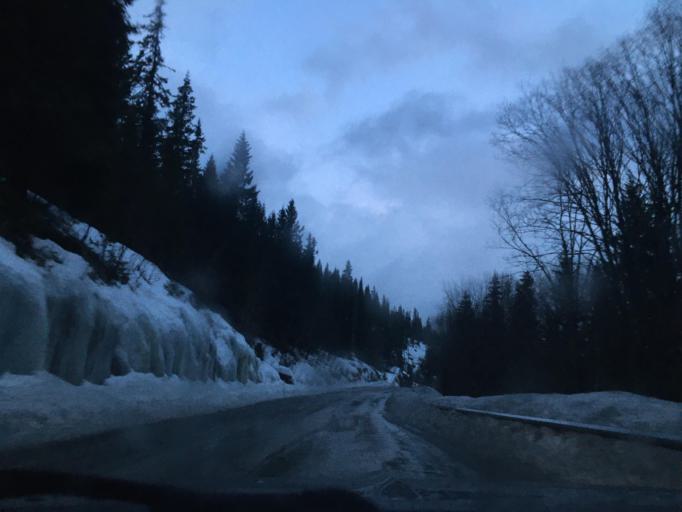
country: NO
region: Nordland
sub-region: Rana
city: Hauknes
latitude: 66.2950
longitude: 13.9187
